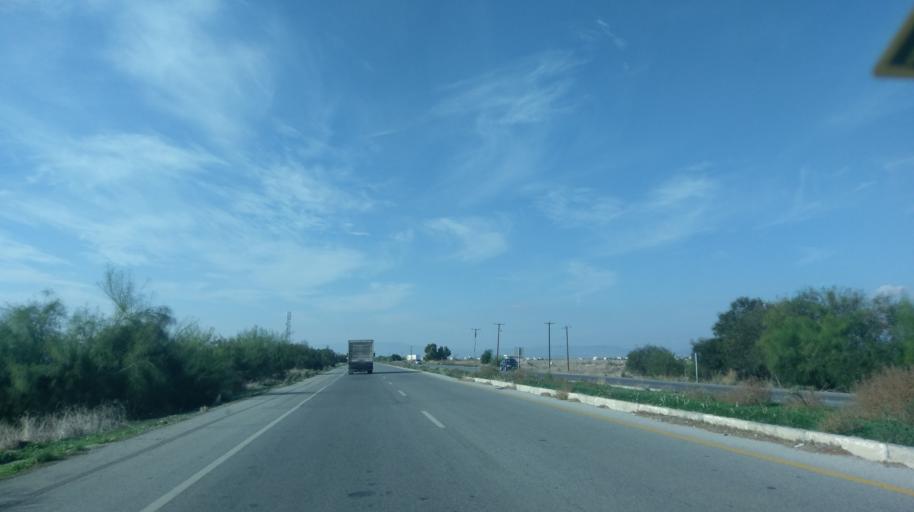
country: CY
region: Ammochostos
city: Acheritou
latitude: 35.1556
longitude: 33.8422
